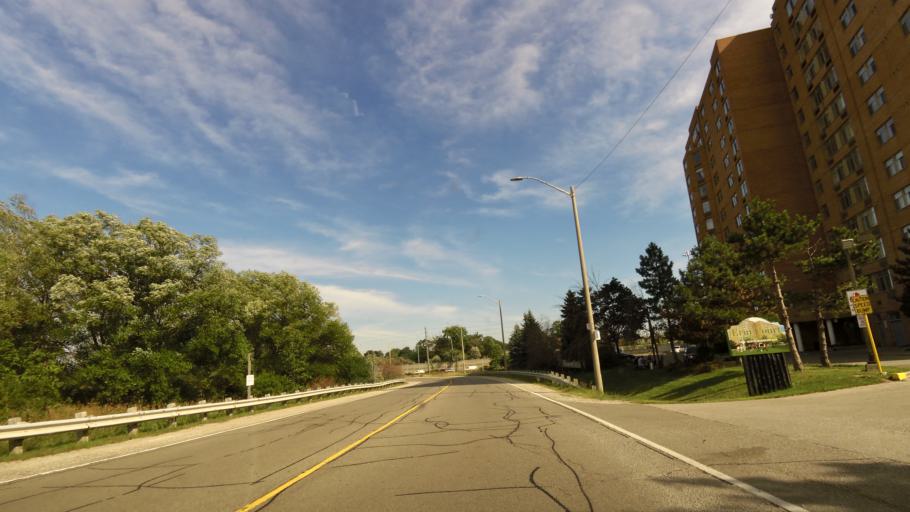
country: CA
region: Ontario
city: Mississauga
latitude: 43.5283
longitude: -79.6465
